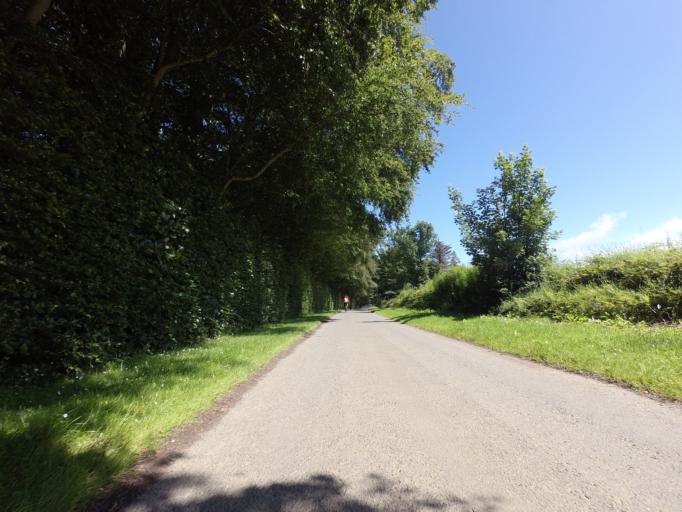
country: GB
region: Scotland
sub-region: Aberdeenshire
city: Macduff
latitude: 57.6275
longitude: -2.4928
